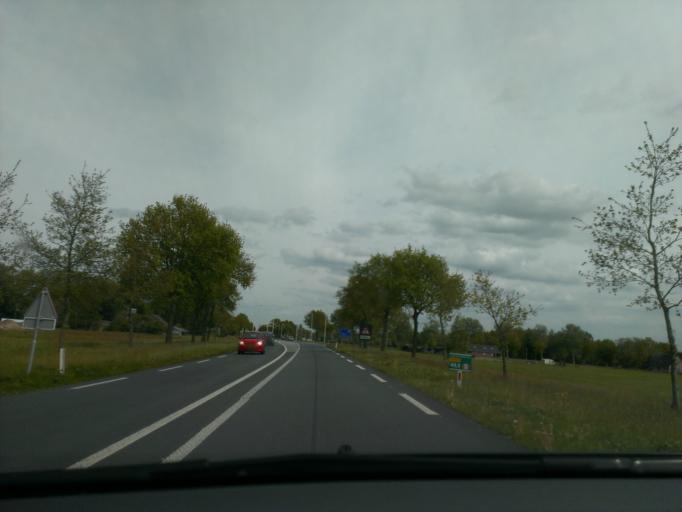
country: NL
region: Gelderland
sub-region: Gemeente Epe
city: Epe
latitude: 52.3380
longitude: 5.9773
